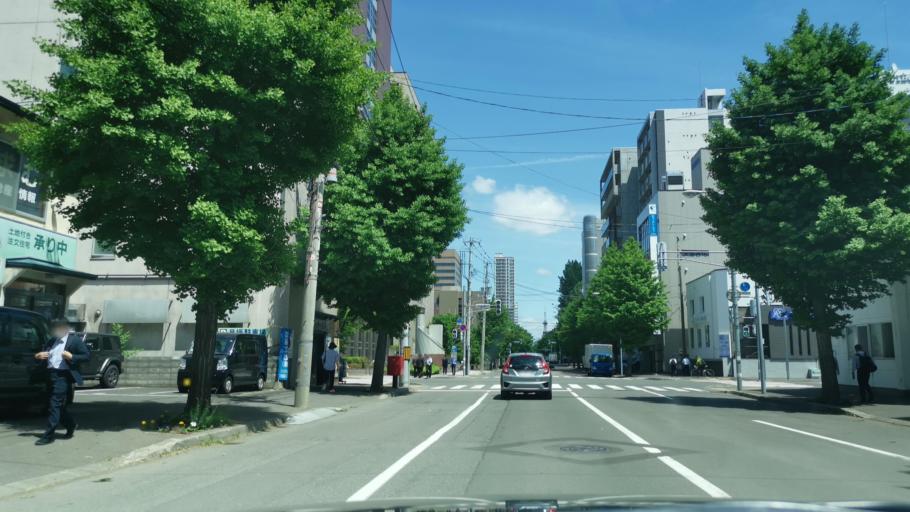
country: JP
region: Hokkaido
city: Sapporo
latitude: 43.0585
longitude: 141.3342
